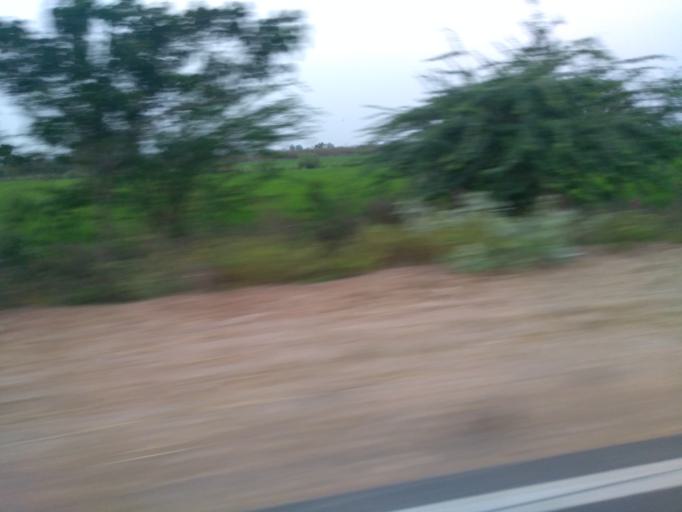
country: IN
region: Andhra Pradesh
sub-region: Cuddapah
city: Proddatur
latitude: 14.7291
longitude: 78.6295
